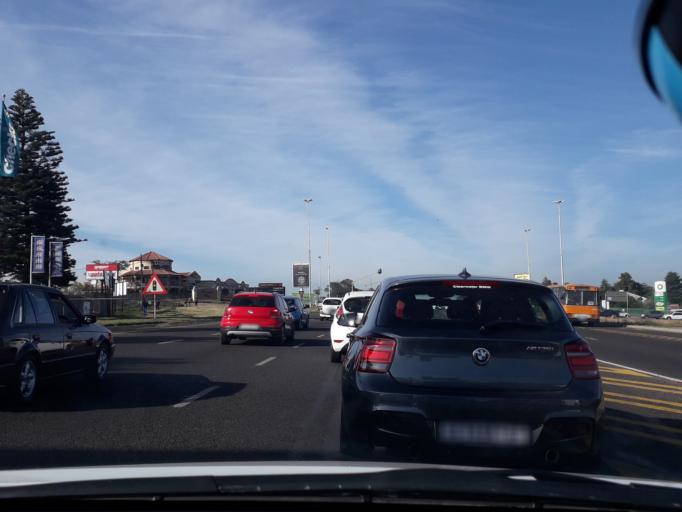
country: ZA
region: Gauteng
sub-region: City of Johannesburg Metropolitan Municipality
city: Roodepoort
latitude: -26.1035
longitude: 27.9257
